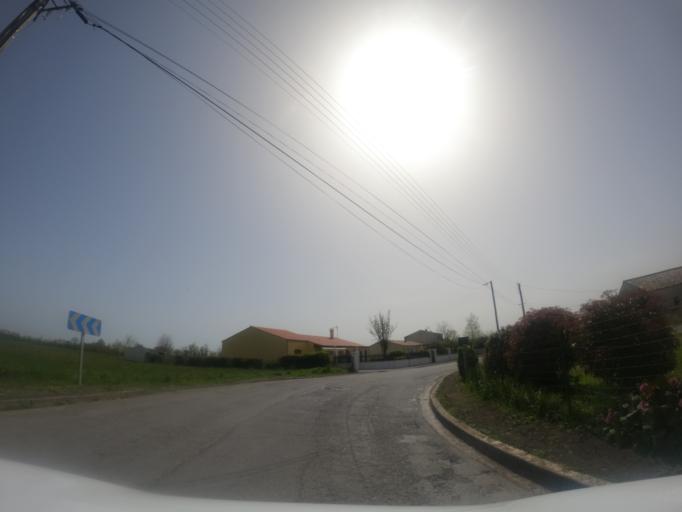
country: FR
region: Pays de la Loire
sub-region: Departement de la Vendee
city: Vix
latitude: 46.3857
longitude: -0.8069
